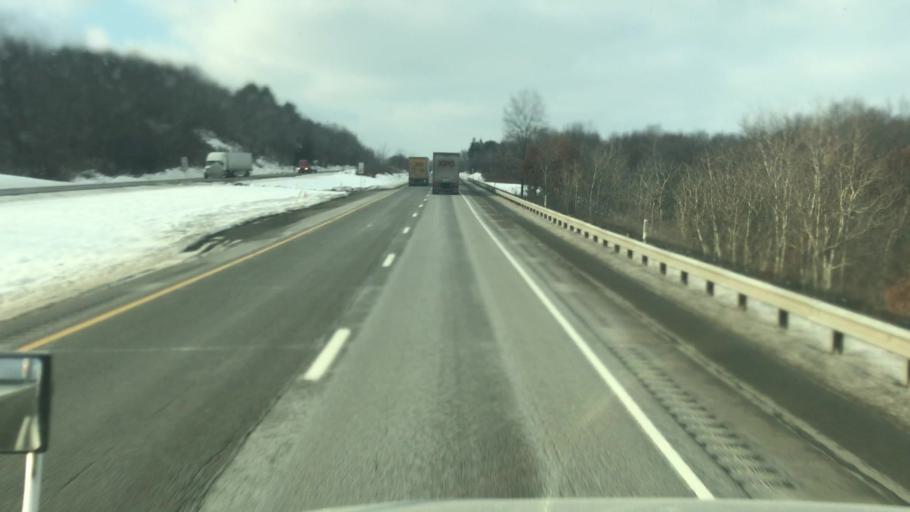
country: US
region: Pennsylvania
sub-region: Clarion County
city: Knox
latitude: 41.1922
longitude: -79.6141
